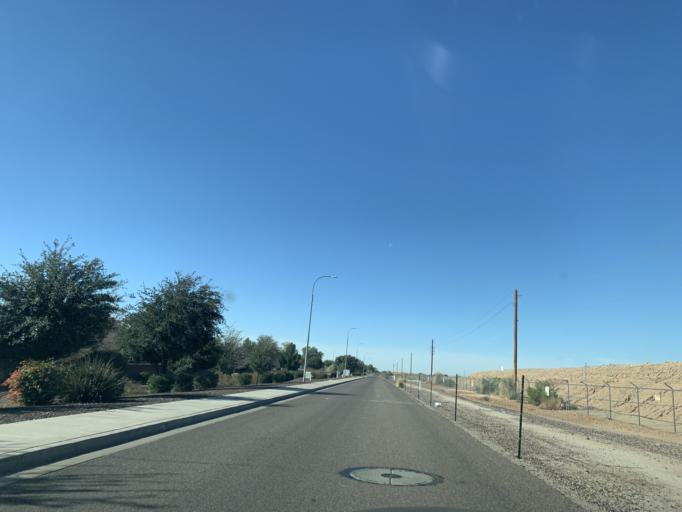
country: US
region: Arizona
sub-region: Maricopa County
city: Laveen
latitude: 33.3994
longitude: -112.1201
